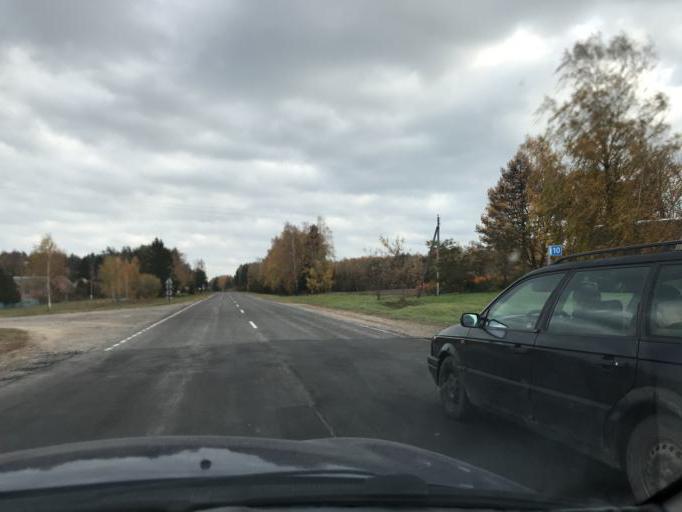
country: BY
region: Grodnenskaya
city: Lida
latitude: 53.7523
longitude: 25.2192
